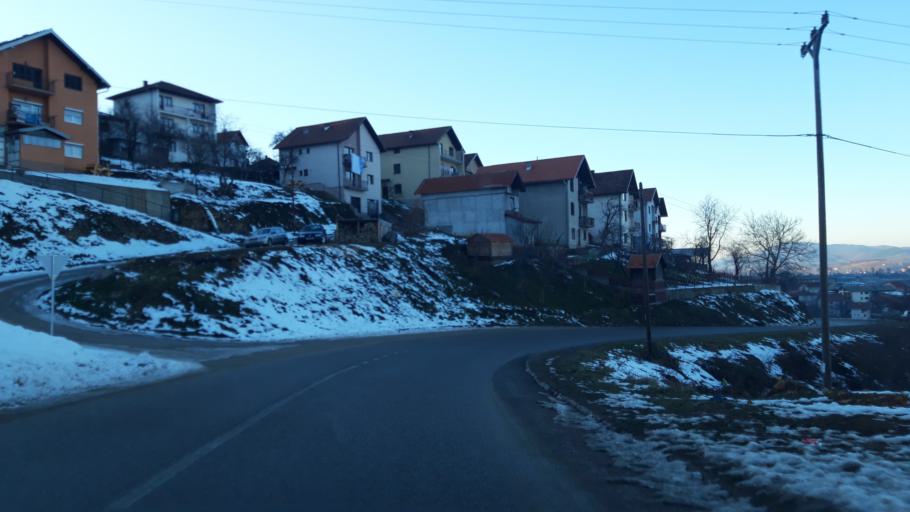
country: BA
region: Republika Srpska
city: Vlasenica
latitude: 44.1793
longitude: 18.9479
